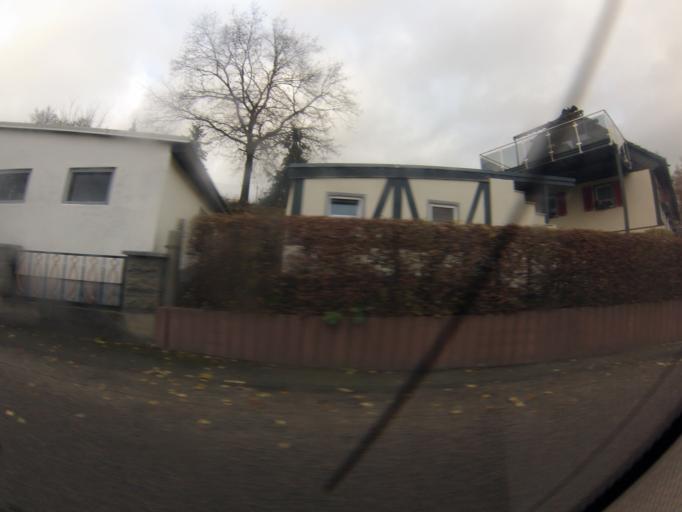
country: DE
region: Thuringia
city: Nobdenitz
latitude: 50.8559
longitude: 12.2867
